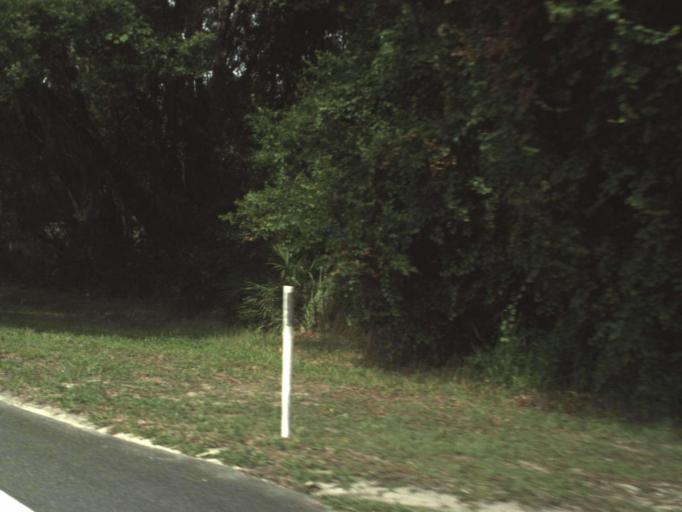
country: US
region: Florida
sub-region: Sumter County
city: Bushnell
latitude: 28.5926
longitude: -82.1470
